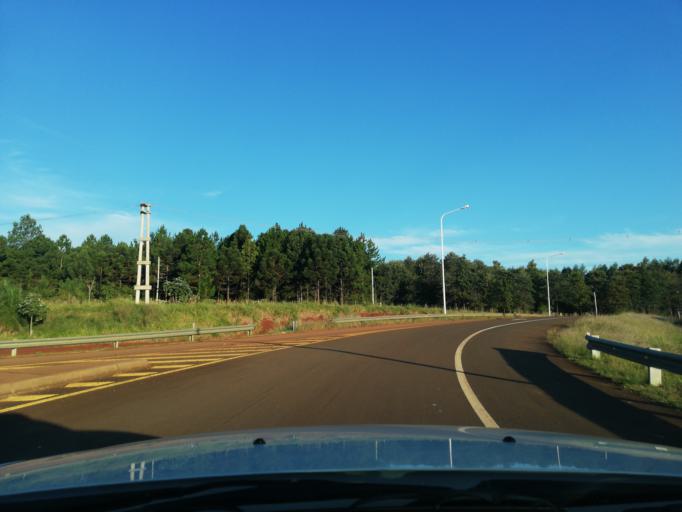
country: AR
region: Misiones
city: Garupa
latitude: -27.4663
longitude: -55.9189
